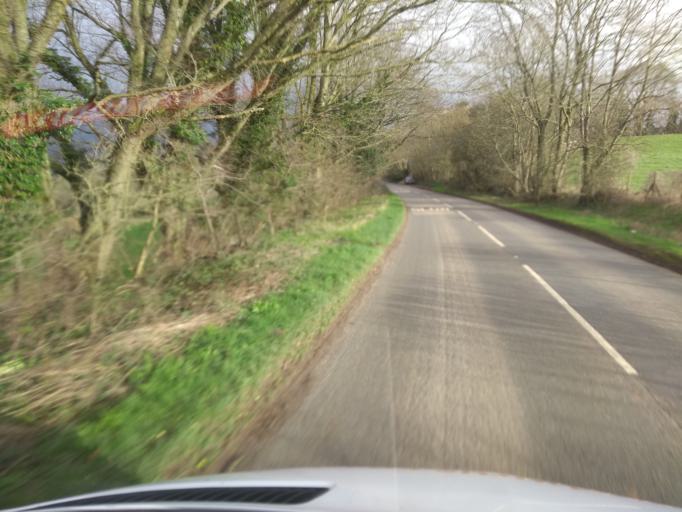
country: GB
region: England
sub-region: Somerset
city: Bruton
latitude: 51.0951
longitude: -2.4655
